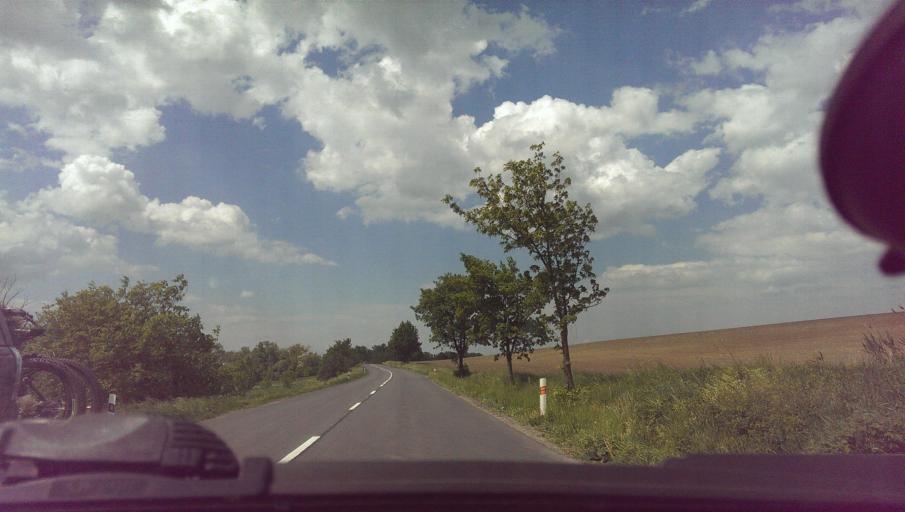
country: CZ
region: Zlin
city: Dolni Nemci
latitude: 48.9713
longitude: 17.5664
